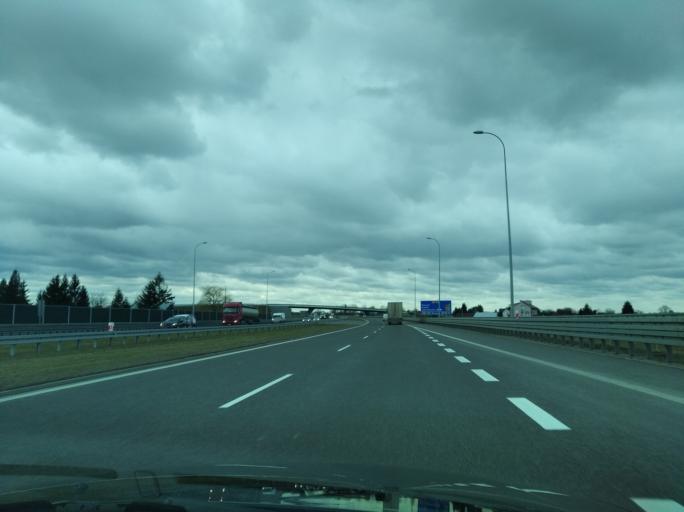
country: PL
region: Subcarpathian Voivodeship
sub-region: Powiat lancucki
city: Lancut
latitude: 50.0990
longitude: 22.2160
